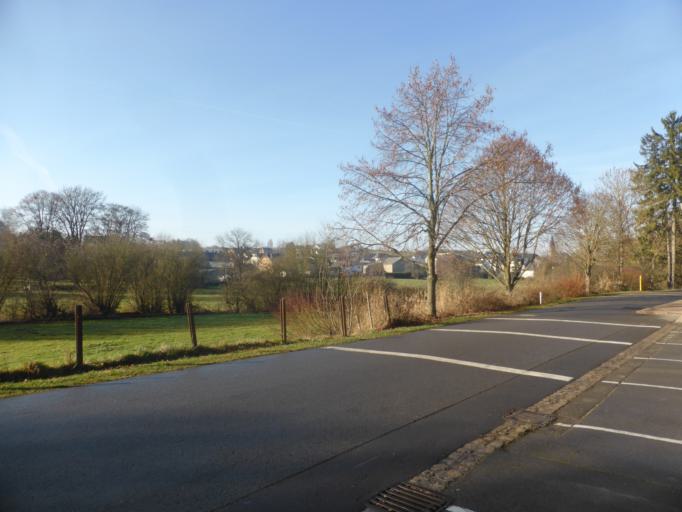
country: LU
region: Luxembourg
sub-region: Canton de Capellen
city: Clemency
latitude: 49.5955
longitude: 5.8807
